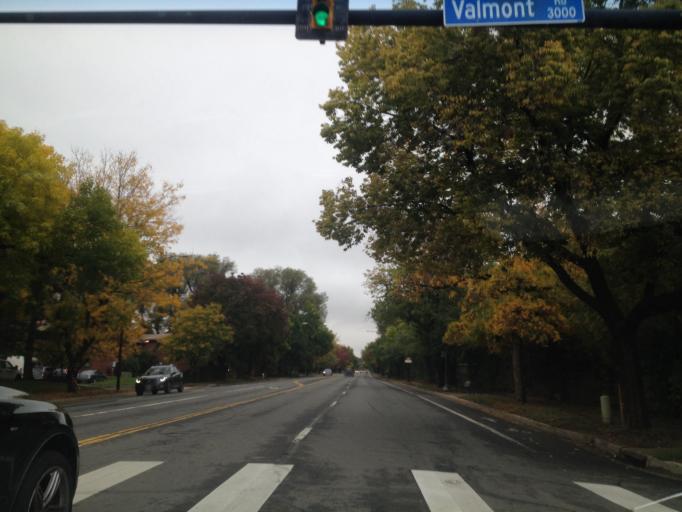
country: US
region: Colorado
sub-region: Boulder County
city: Boulder
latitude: 40.0293
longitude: -105.2537
